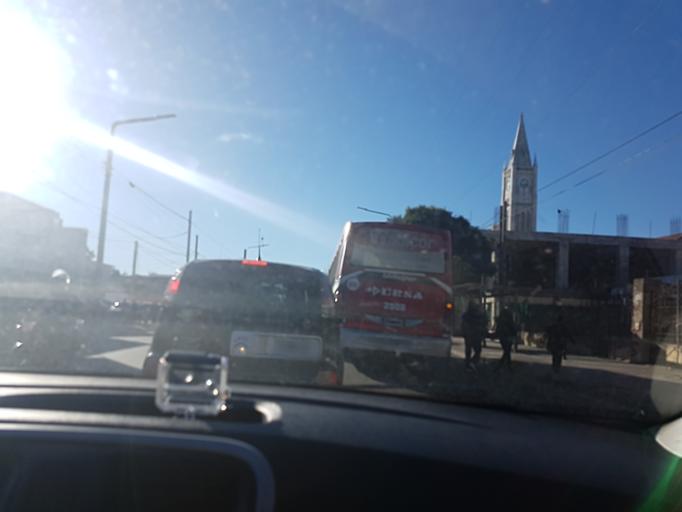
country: AR
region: Cordoba
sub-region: Departamento de Capital
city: Cordoba
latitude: -31.3945
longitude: -64.2019
